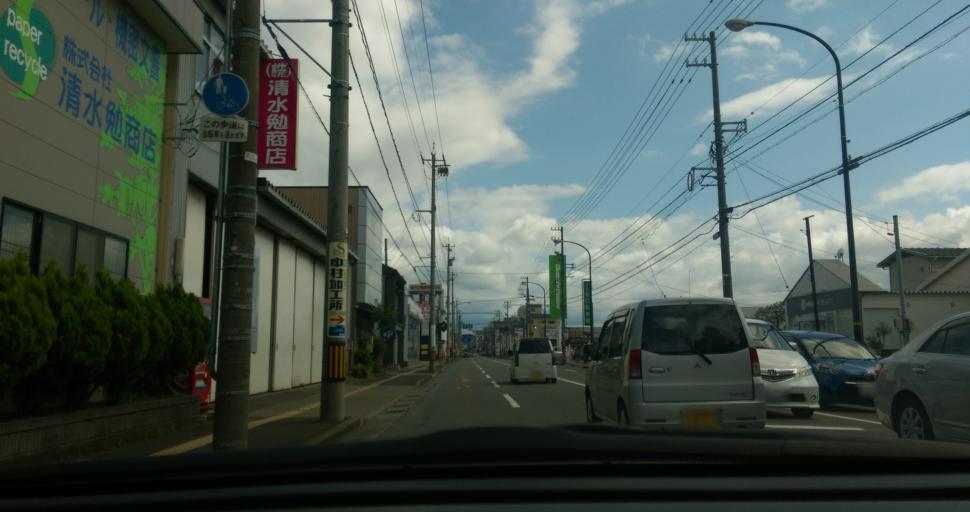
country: JP
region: Fukui
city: Fukui-shi
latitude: 36.0857
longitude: 136.2090
